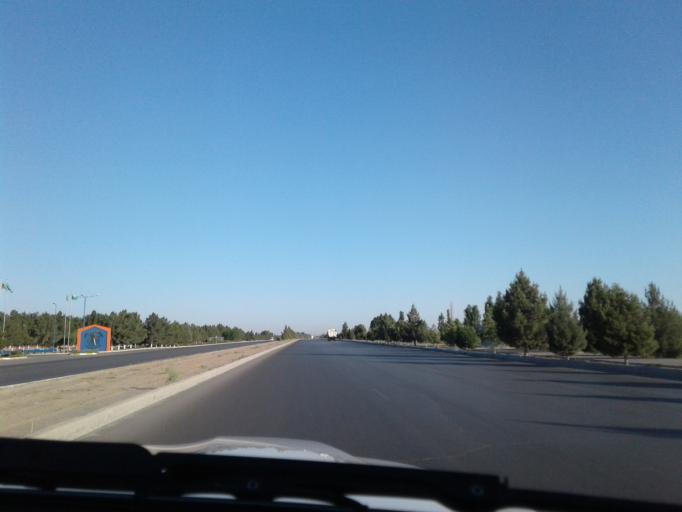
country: TM
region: Ahal
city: Abadan
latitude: 38.0622
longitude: 58.2612
